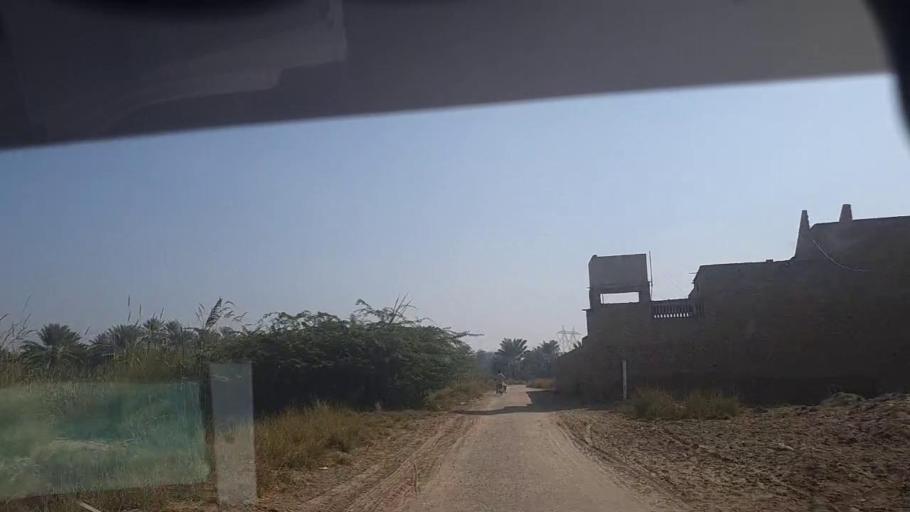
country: PK
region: Sindh
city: Khairpur
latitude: 27.4590
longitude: 68.7406
